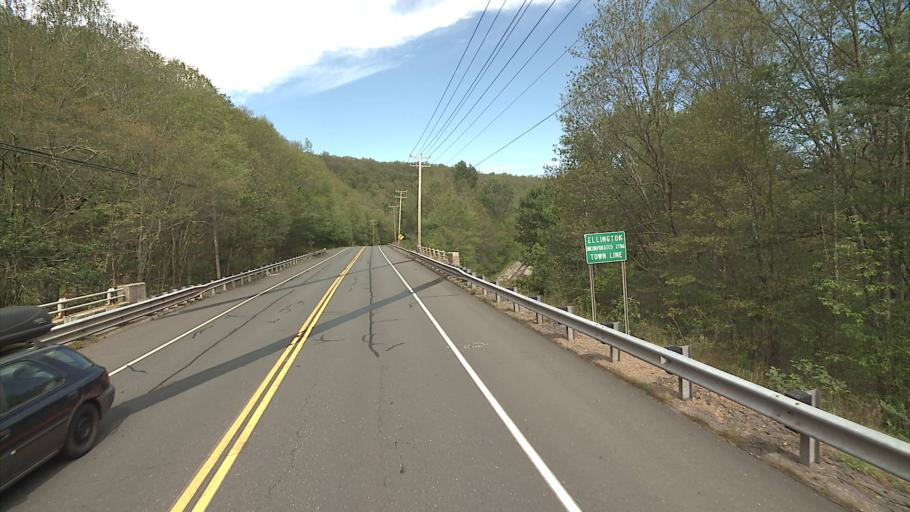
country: US
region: Connecticut
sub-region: Tolland County
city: Stafford Springs
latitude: 41.9293
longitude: -72.3076
